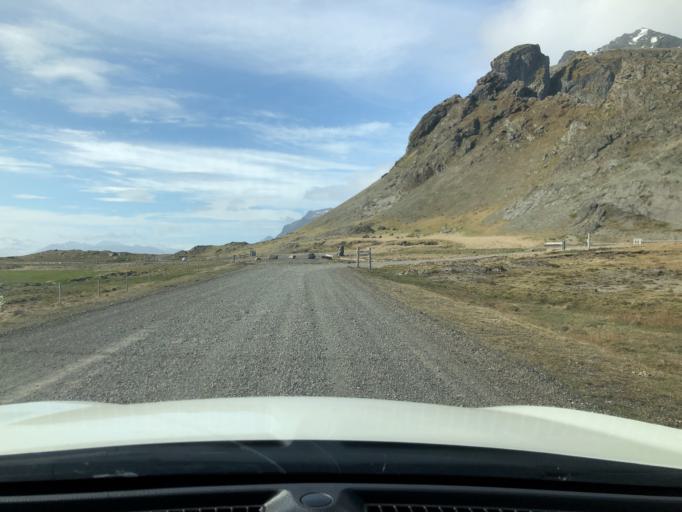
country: IS
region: East
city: Hoefn
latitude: 64.2541
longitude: -14.9938
